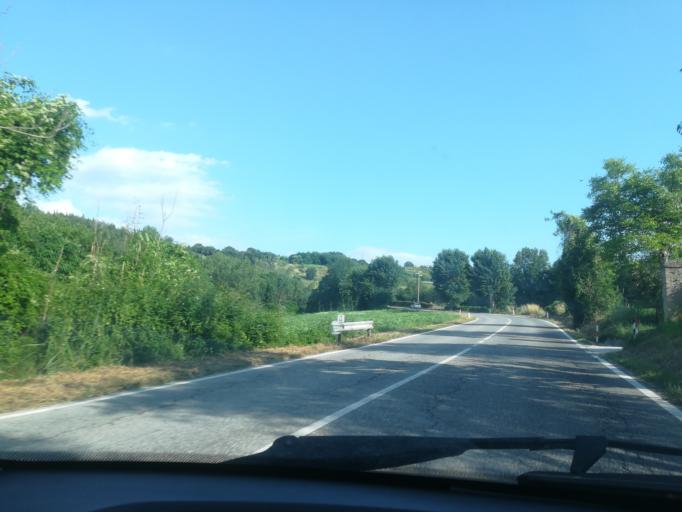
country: IT
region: The Marches
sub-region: Provincia di Macerata
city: Villa Potenza
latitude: 43.3170
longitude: 13.4265
